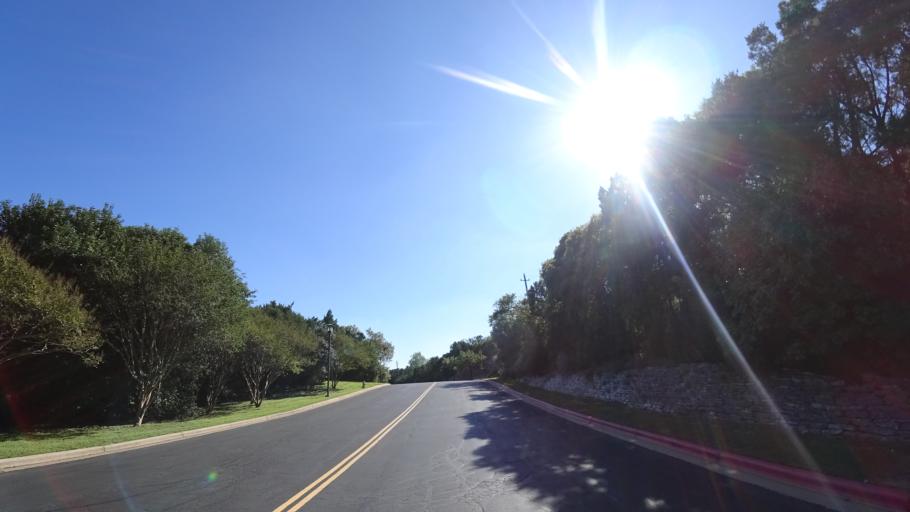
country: US
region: Texas
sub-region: Travis County
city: Rollingwood
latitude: 30.2570
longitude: -97.7973
